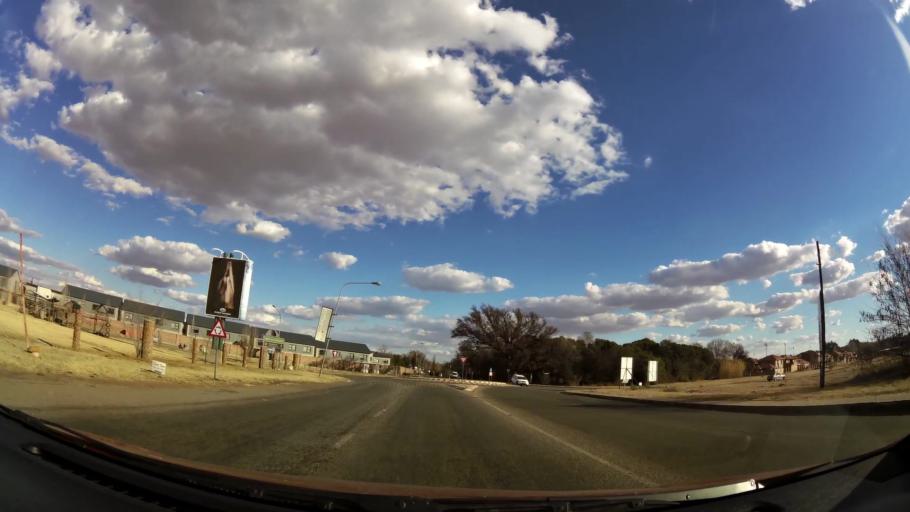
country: ZA
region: North-West
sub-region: Dr Kenneth Kaunda District Municipality
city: Potchefstroom
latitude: -26.6807
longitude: 27.1029
